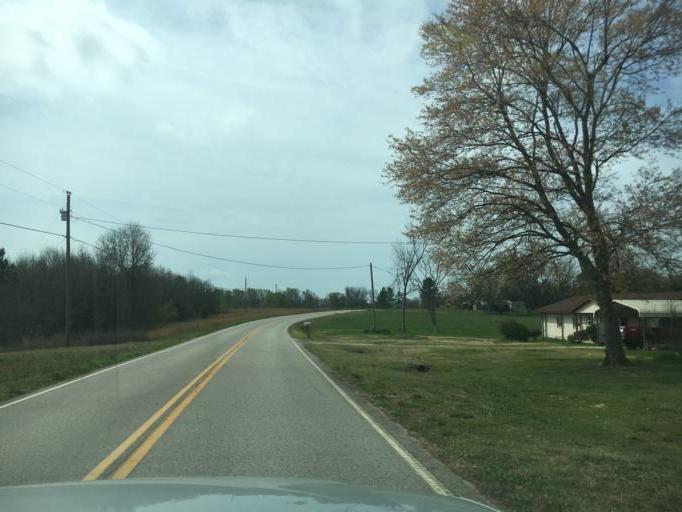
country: US
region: Georgia
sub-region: Hart County
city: Royston
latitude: 34.3202
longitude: -83.0443
